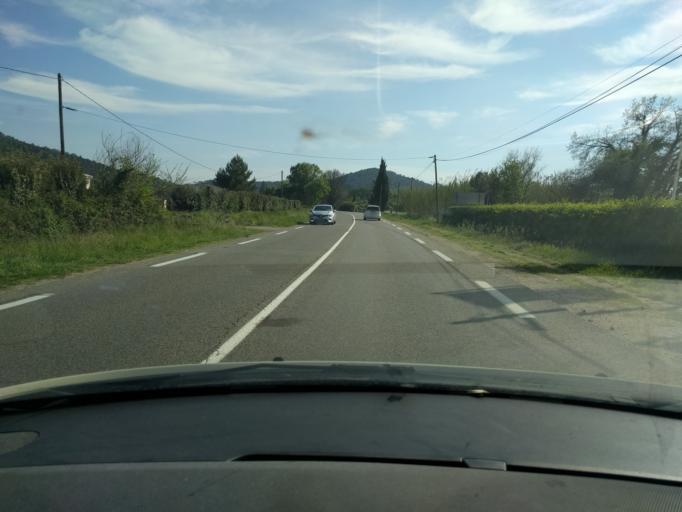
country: FR
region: Provence-Alpes-Cote d'Azur
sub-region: Departement du Var
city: Pierrefeu-du-Var
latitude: 43.1790
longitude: 6.1180
